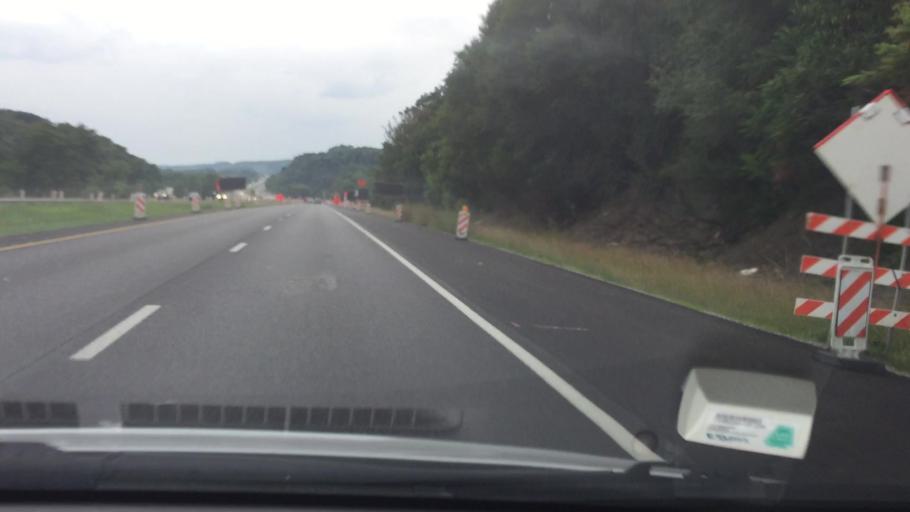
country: US
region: Pennsylvania
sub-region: Allegheny County
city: Brackenridge
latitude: 40.6383
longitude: -79.7236
